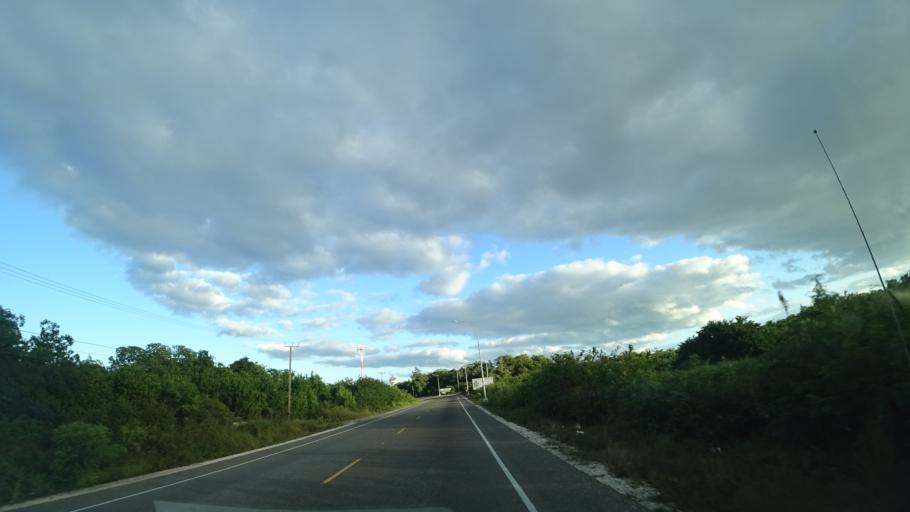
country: BZ
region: Belize
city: Belize City
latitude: 17.5428
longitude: -88.2549
